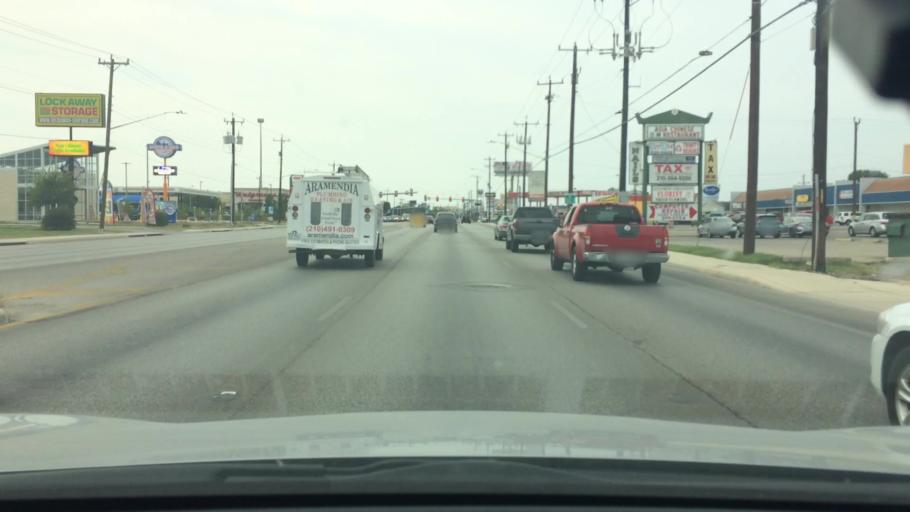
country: US
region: Texas
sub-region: Bexar County
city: Leon Valley
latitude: 29.4654
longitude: -98.6455
